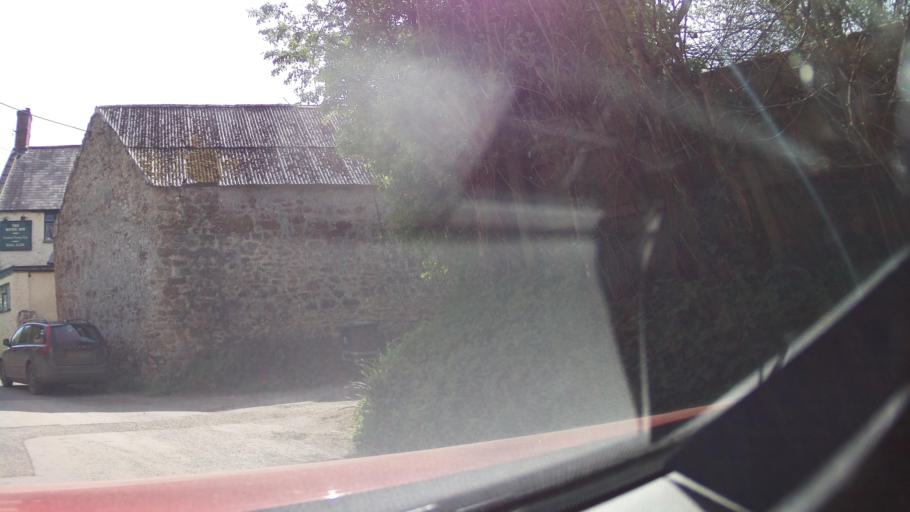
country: GB
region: England
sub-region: Dorset
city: Sherborne
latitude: 50.9840
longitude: -2.5352
